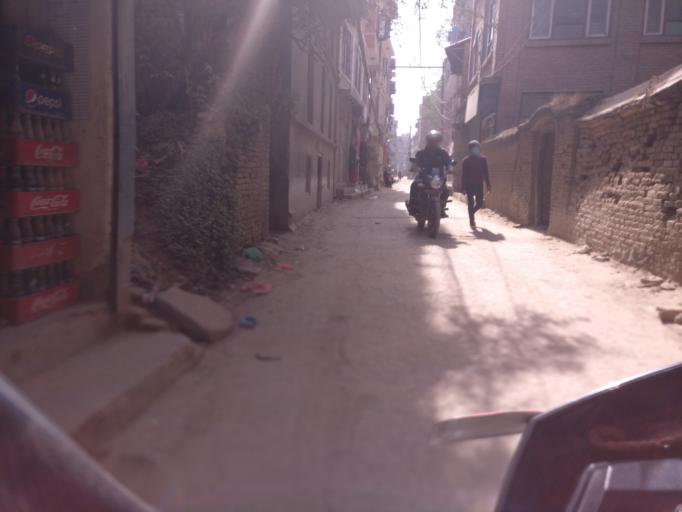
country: NP
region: Central Region
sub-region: Bagmati Zone
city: Patan
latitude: 27.6721
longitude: 85.3233
